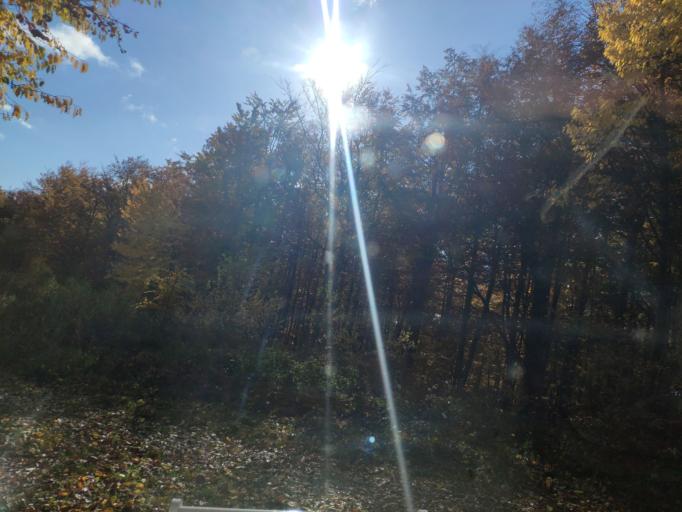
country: SK
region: Kosicky
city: Moldava nad Bodvou
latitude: 48.7231
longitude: 21.0358
